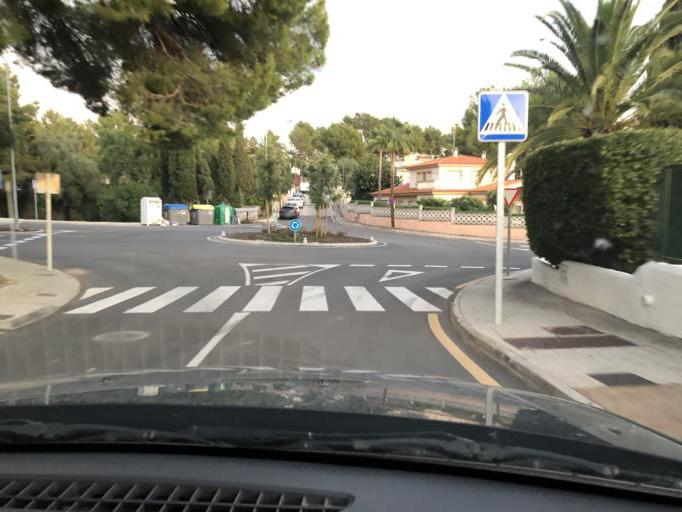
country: ES
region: Balearic Islands
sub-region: Illes Balears
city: Santa Ponsa
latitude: 39.5268
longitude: 2.4819
